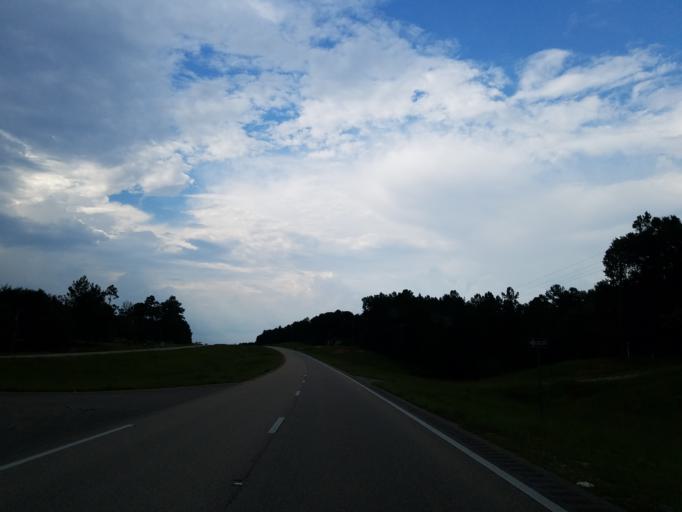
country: US
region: Mississippi
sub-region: Wayne County
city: Belmont
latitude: 31.4940
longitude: -88.4923
